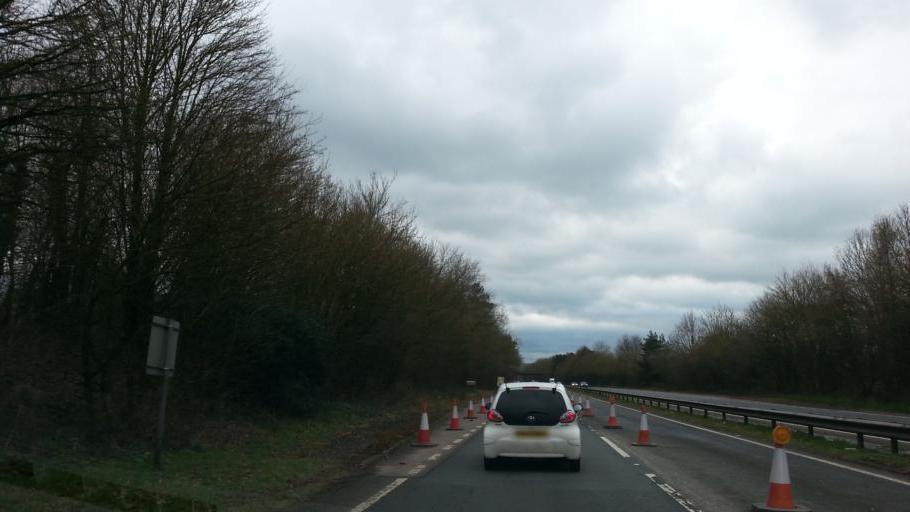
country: GB
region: England
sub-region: Devon
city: Cullompton
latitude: 50.9192
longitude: -3.4140
